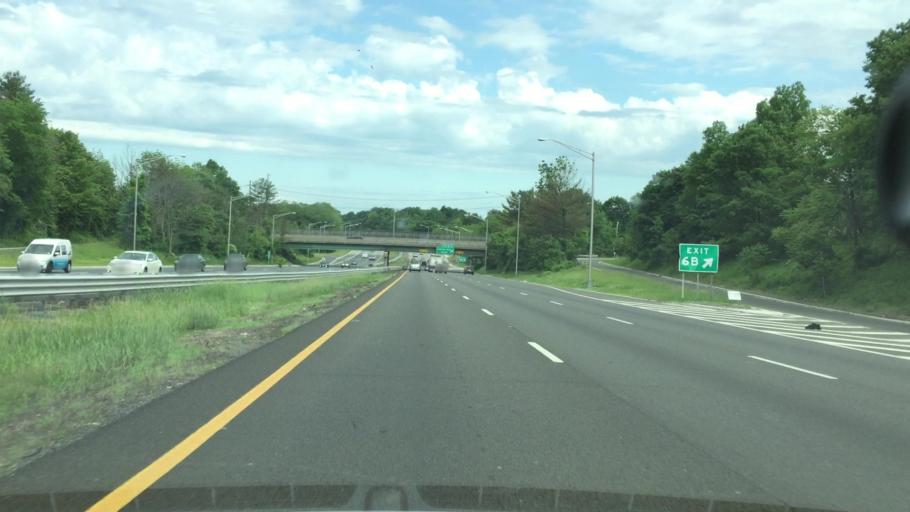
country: US
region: New Jersey
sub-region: Essex County
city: Roseland
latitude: 40.8054
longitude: -74.2836
